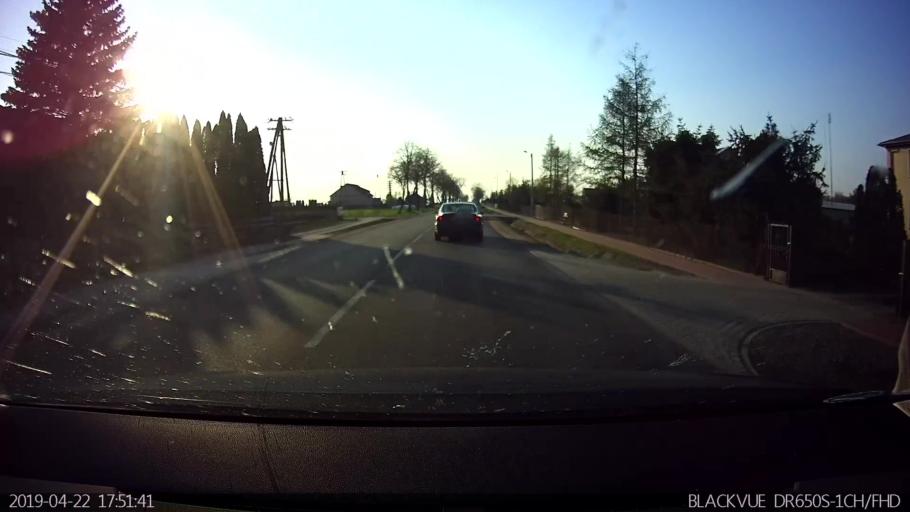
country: PL
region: Masovian Voivodeship
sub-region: Powiat wegrowski
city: Wegrow
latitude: 52.4364
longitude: 21.9909
